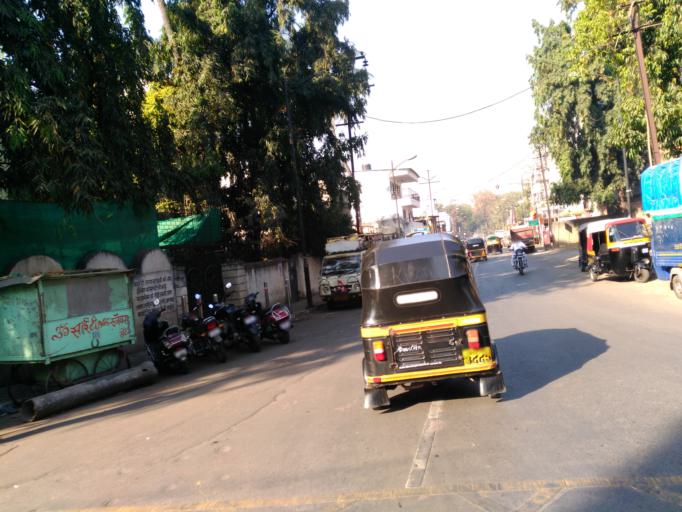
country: IN
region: Maharashtra
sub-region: Pune Division
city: Pune
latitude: 18.5074
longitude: 73.8723
